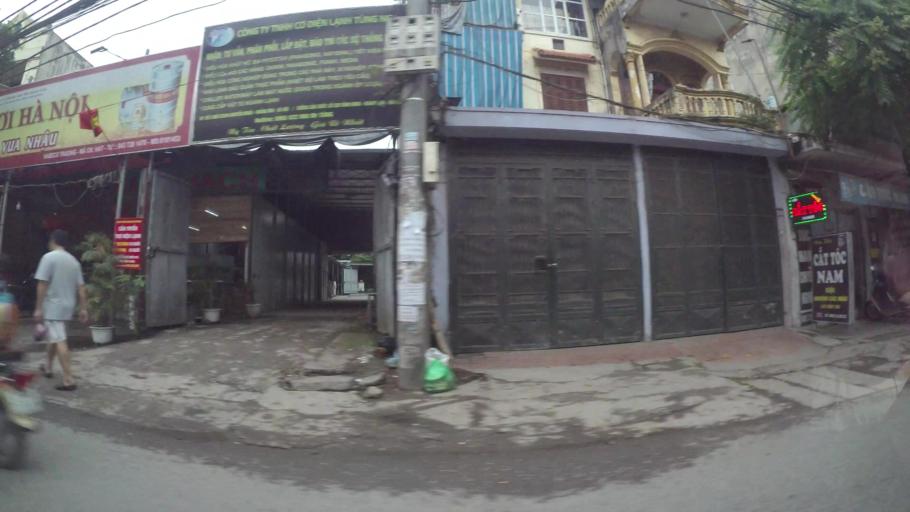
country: VN
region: Ha Noi
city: Hai BaTrung
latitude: 20.9913
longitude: 105.8791
